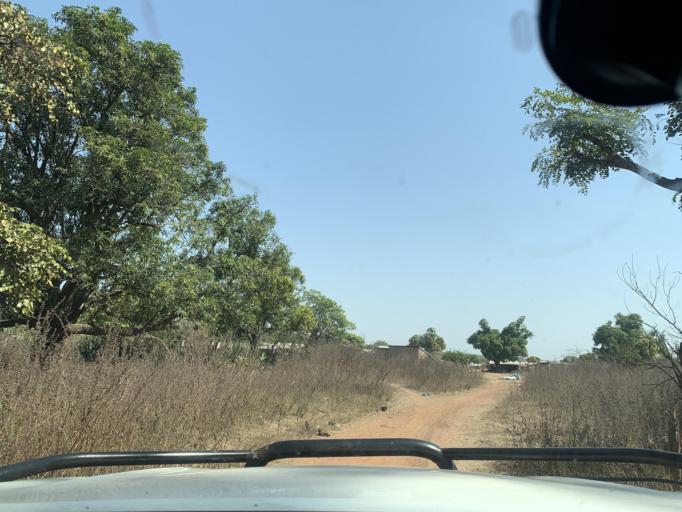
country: ML
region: Sikasso
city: Kolondieba
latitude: 10.8293
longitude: -6.7244
